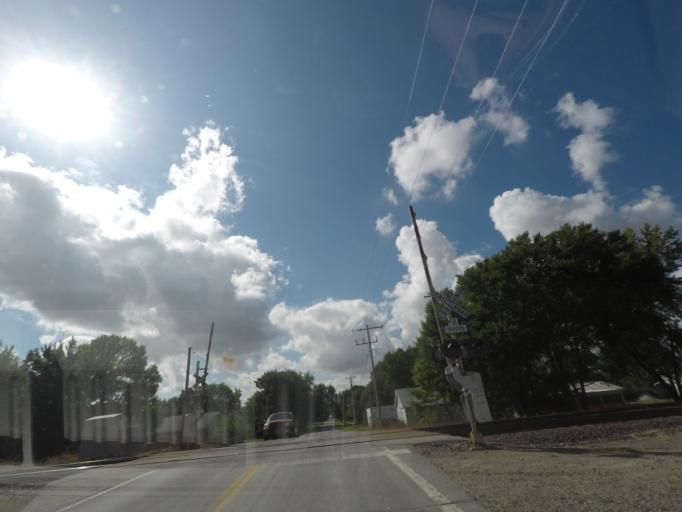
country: US
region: Iowa
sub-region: Story County
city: Nevada
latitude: 42.0193
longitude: -93.3194
